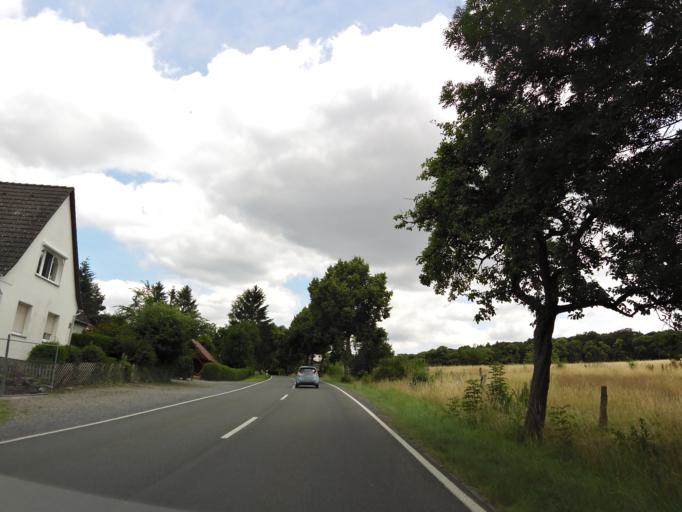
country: DE
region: Lower Saxony
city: Boffzen
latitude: 51.7635
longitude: 9.4094
